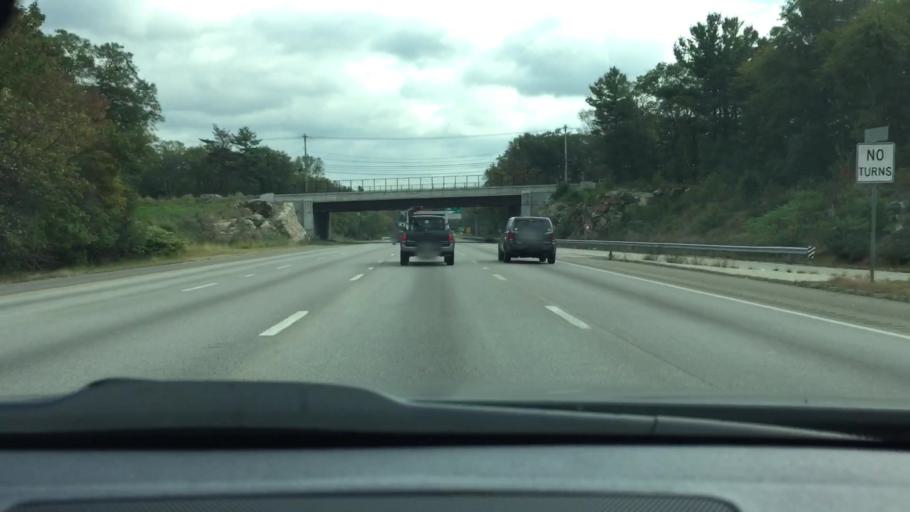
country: US
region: Massachusetts
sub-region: Norfolk County
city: Westwood
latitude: 42.2444
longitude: -71.2062
